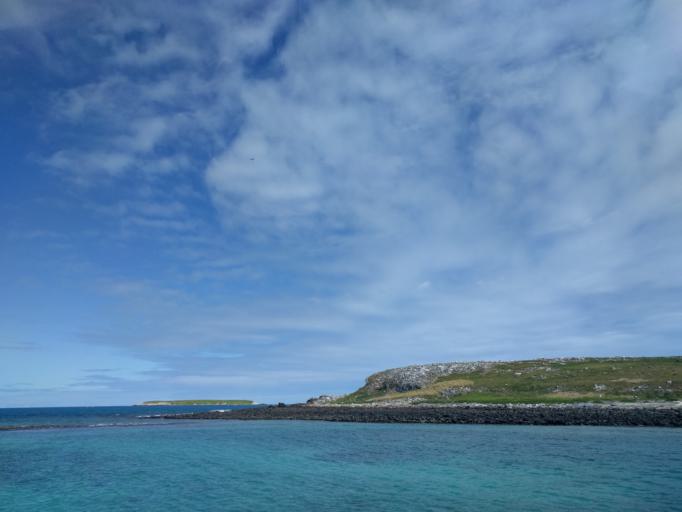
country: BR
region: Bahia
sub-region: Nova Vicosa
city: Nova Vicosa
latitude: -17.9695
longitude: -38.7093
